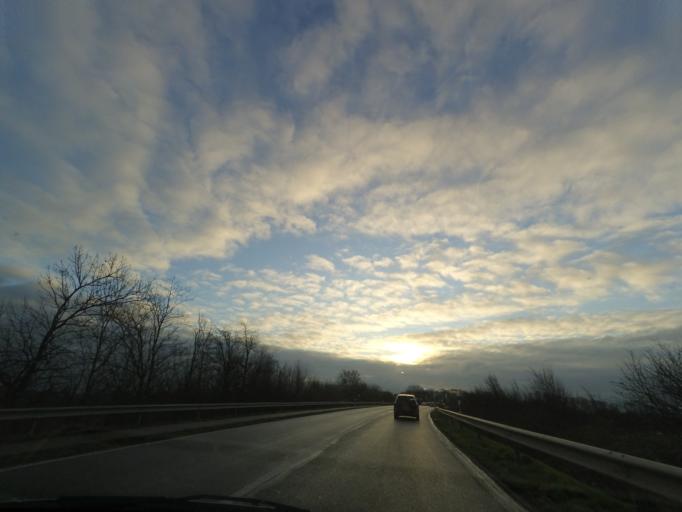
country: DE
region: North Rhine-Westphalia
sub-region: Regierungsbezirk Dusseldorf
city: Grevenbroich
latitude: 51.1101
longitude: 6.5624
